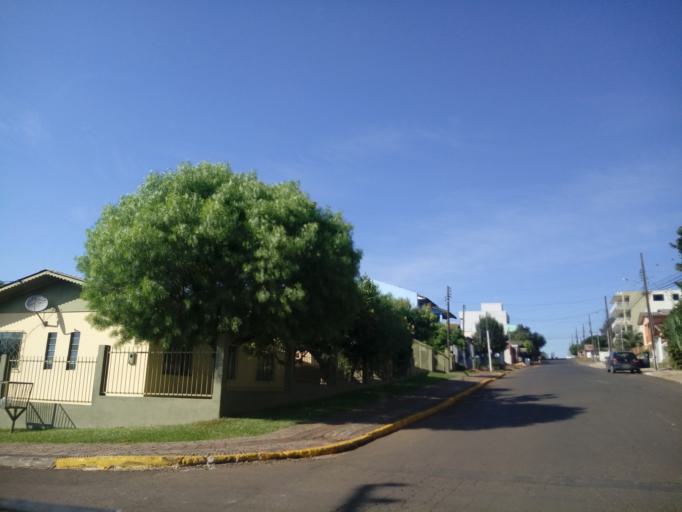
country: BR
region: Santa Catarina
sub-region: Chapeco
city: Chapeco
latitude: -27.0981
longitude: -52.6696
